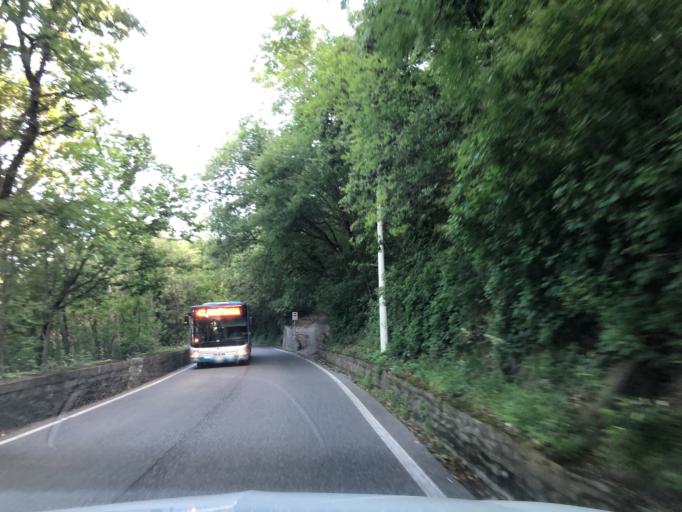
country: IT
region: Friuli Venezia Giulia
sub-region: Provincia di Trieste
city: Prosecco-Contovello
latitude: 45.6939
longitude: 13.7438
